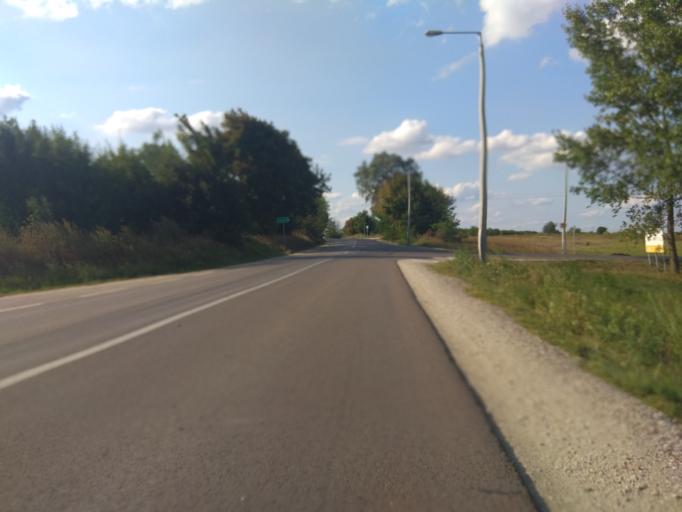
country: HU
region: Borsod-Abauj-Zemplen
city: Hejobaba
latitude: 47.8906
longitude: 20.8956
